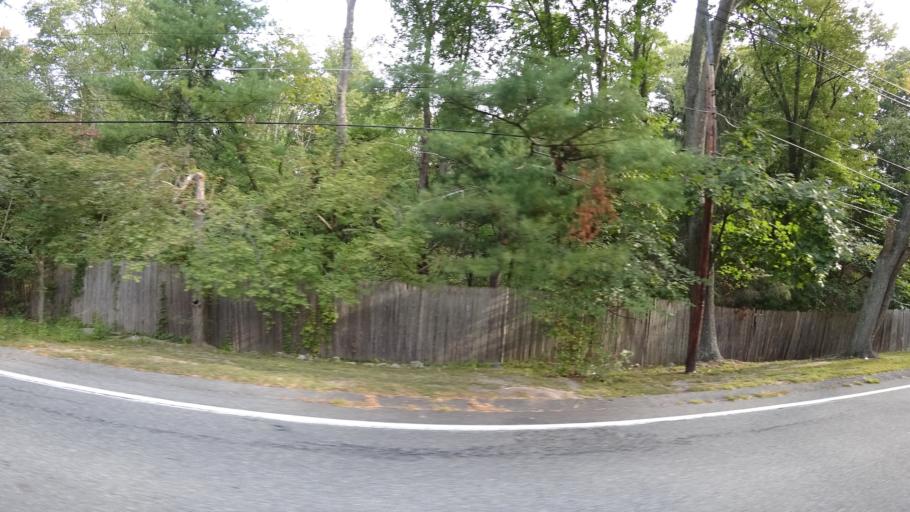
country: US
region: Massachusetts
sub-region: Norfolk County
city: Needham
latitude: 42.2573
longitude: -71.2345
